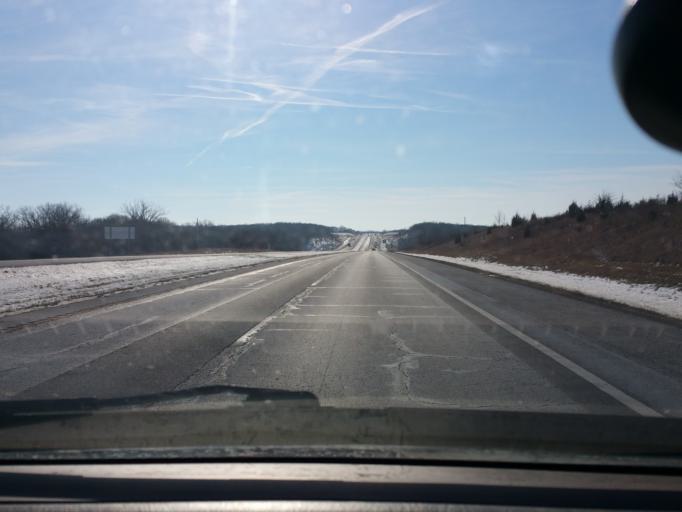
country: US
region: Missouri
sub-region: Harrison County
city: Bethany
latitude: 40.2239
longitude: -94.0131
